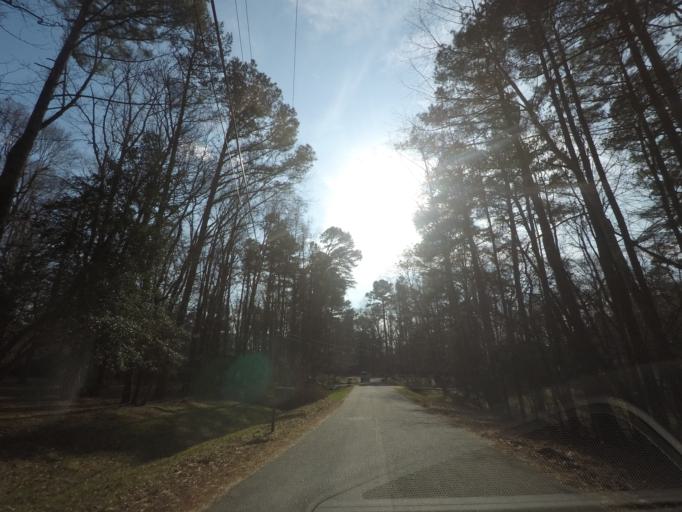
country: US
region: North Carolina
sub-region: Durham County
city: Durham
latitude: 36.0814
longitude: -78.9666
